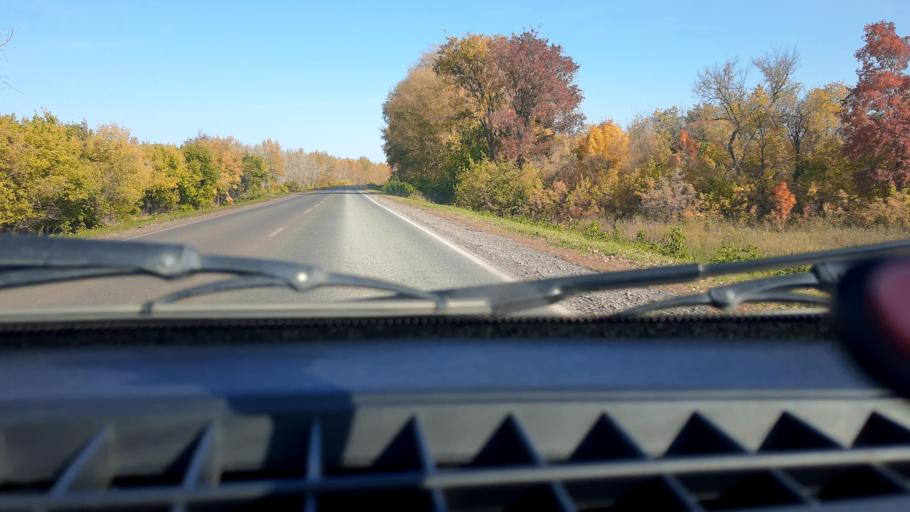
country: RU
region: Bashkortostan
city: Chishmy
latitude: 54.5698
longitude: 55.5304
